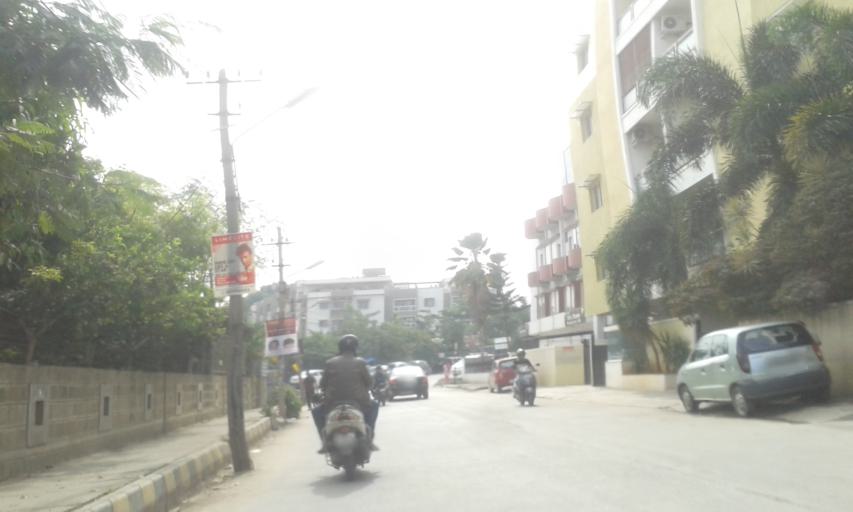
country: IN
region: Karnataka
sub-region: Bangalore Urban
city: Bangalore
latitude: 12.9315
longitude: 77.6336
